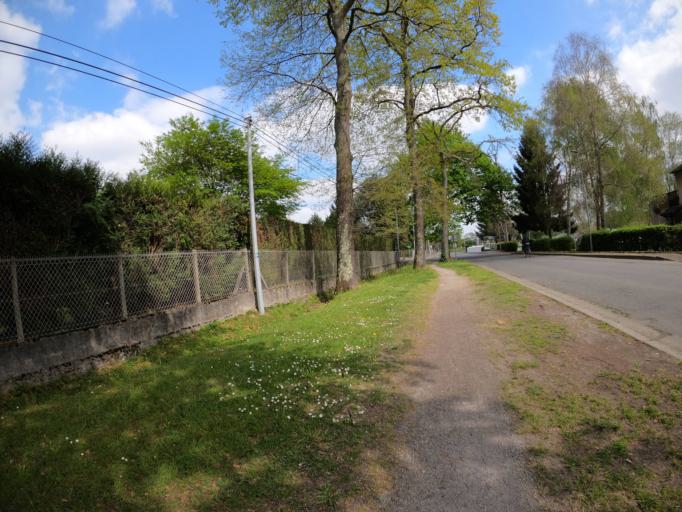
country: FR
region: Aquitaine
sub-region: Departement des Pyrenees-Atlantiques
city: Lons
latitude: 43.3363
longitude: -0.3875
